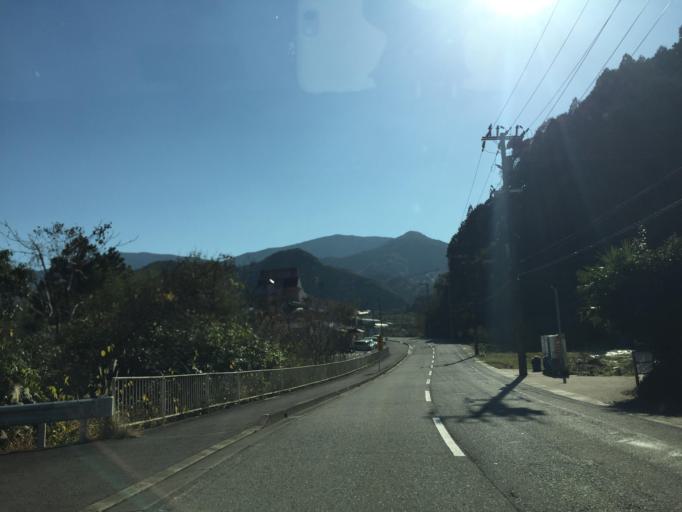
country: JP
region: Wakayama
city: Iwade
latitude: 34.1500
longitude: 135.3461
